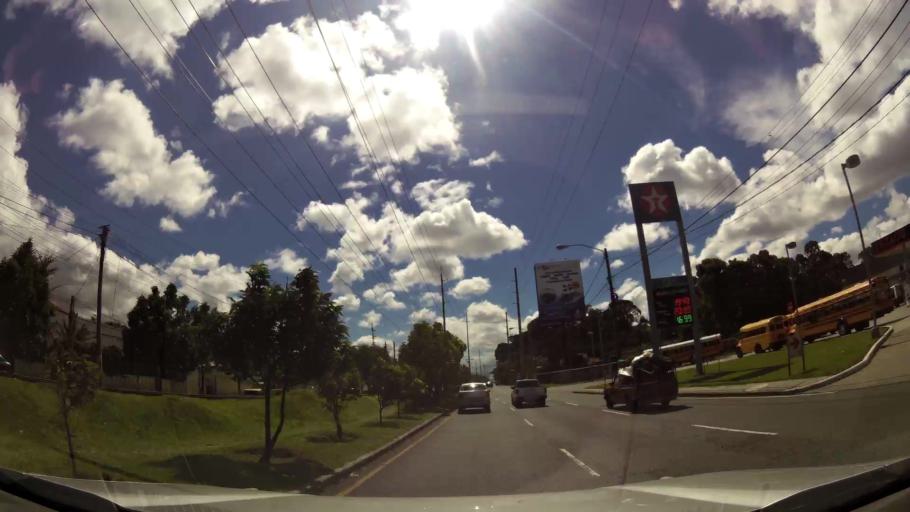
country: GT
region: Guatemala
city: Santa Catarina Pinula
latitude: 14.5928
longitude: -90.5411
